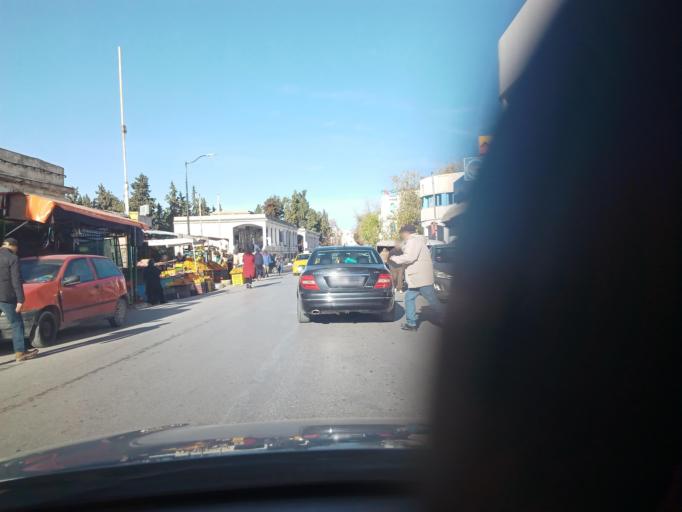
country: TN
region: Kef
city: El Kef
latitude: 36.1782
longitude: 8.7139
